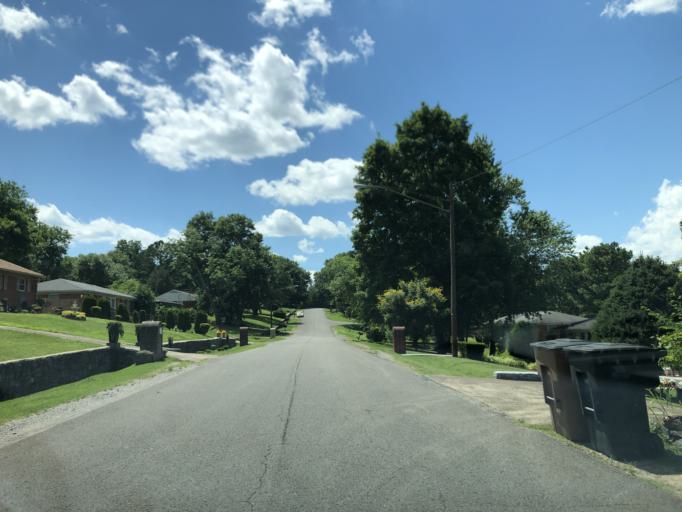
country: US
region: Tennessee
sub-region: Davidson County
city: Nashville
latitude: 36.1745
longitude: -86.7238
